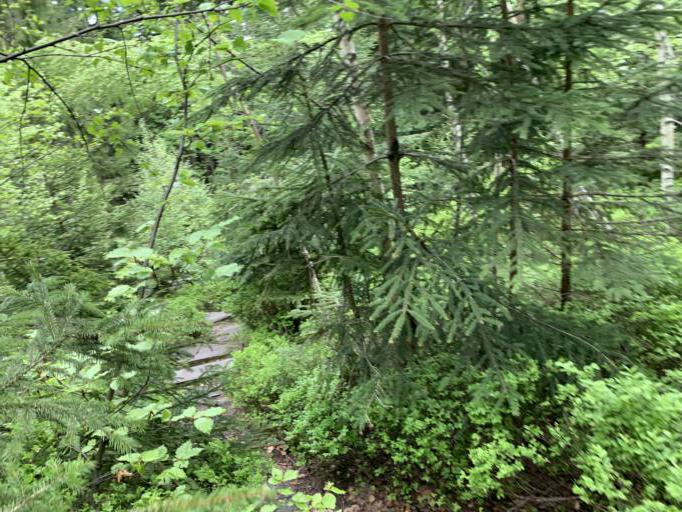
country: PL
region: Lower Silesian Voivodeship
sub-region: Powiat klodzki
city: Radkow
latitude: 50.4609
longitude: 16.3501
